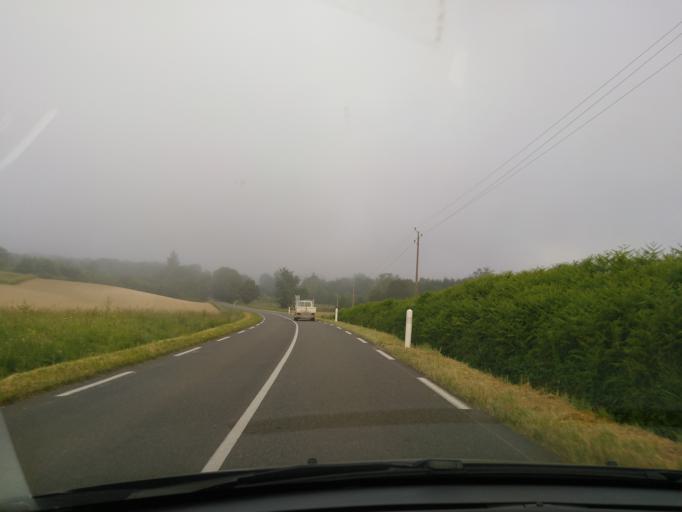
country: FR
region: Midi-Pyrenees
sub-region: Departement du Gers
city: Eauze
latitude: 43.8778
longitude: 0.1615
